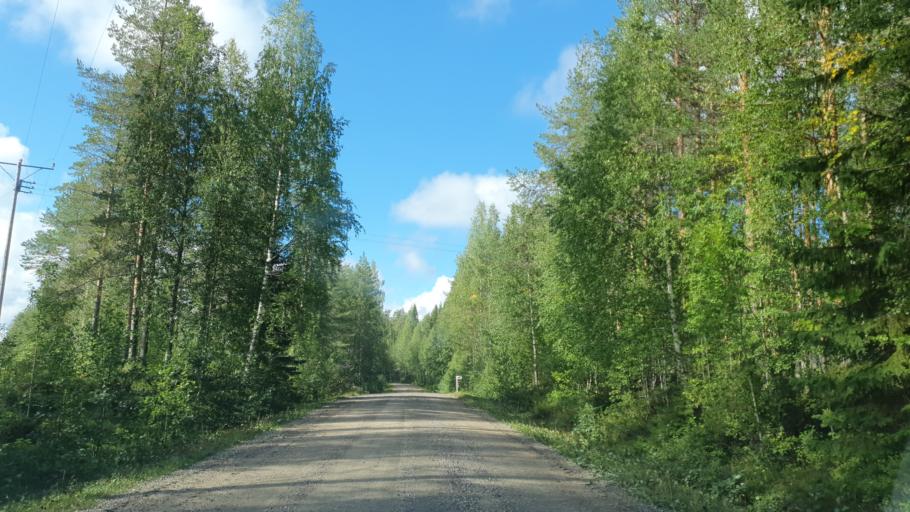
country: FI
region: Kainuu
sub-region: Kehys-Kainuu
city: Kuhmo
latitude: 64.0381
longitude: 29.1422
